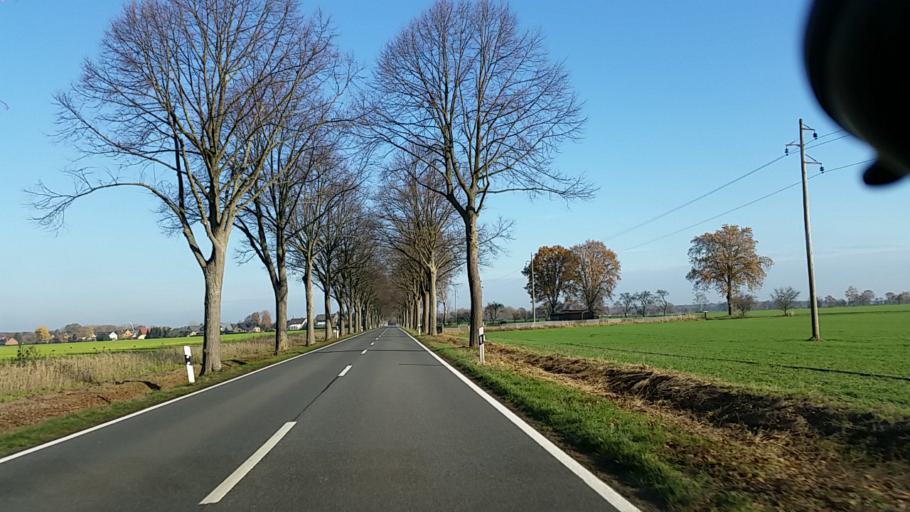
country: DE
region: Lower Saxony
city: Bergfeld
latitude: 52.5363
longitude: 10.8359
